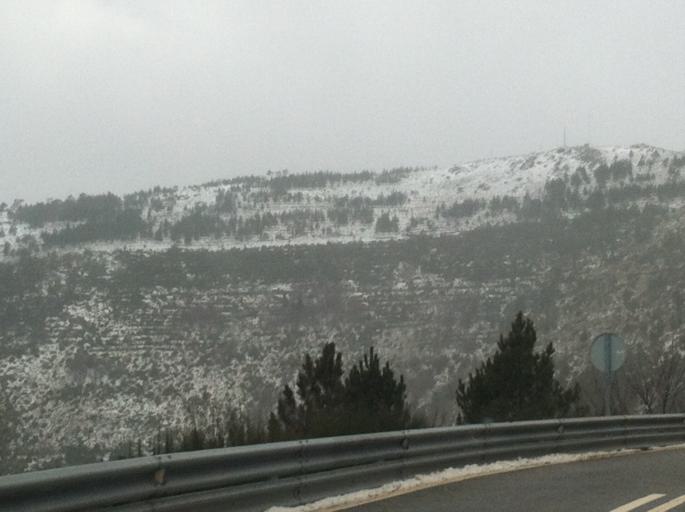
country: PT
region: Castelo Branco
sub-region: Covilha
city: Covilha
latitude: 40.2862
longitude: -7.5258
